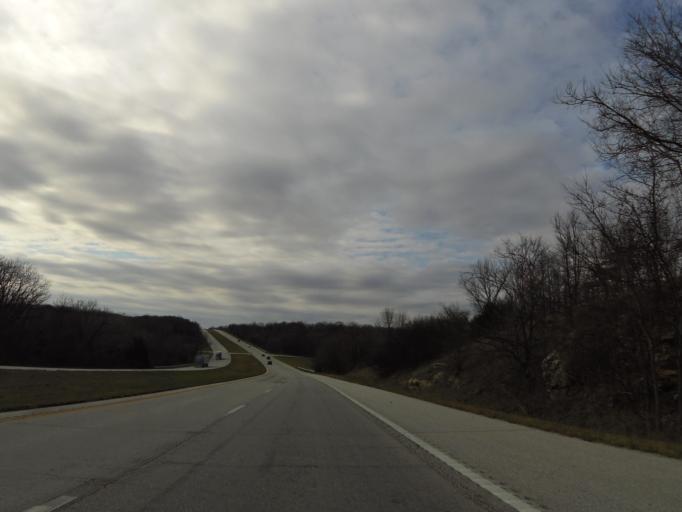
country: US
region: Missouri
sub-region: Marion County
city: Hannibal
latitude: 39.7436
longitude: -91.4259
